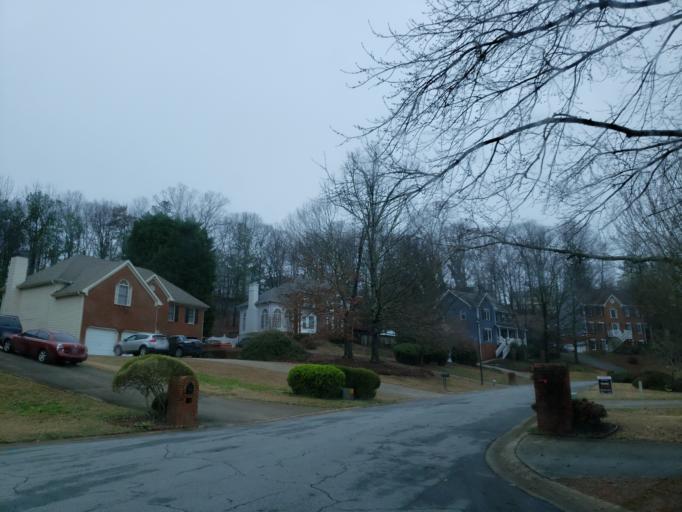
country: US
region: Georgia
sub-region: Cobb County
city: Fair Oaks
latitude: 33.9283
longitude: -84.5765
